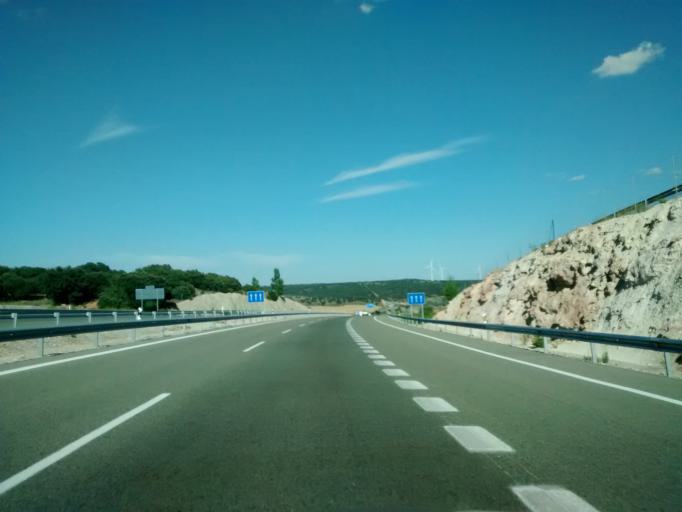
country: ES
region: Castille-La Mancha
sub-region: Provincia de Guadalajara
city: Sauca
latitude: 41.0156
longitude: -2.5478
